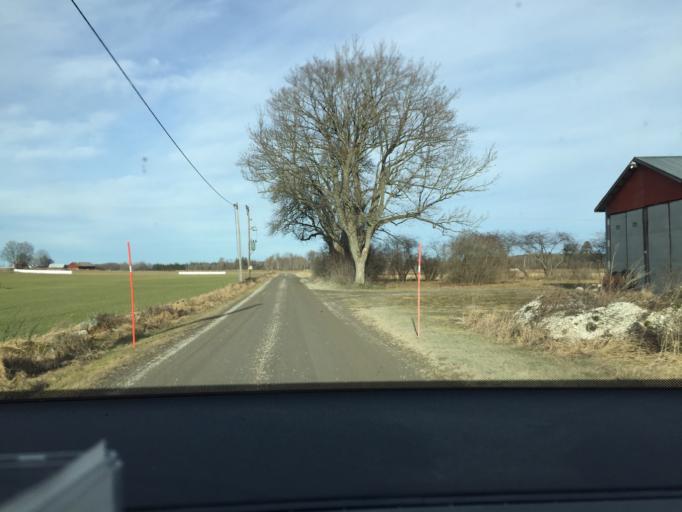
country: SE
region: OErebro
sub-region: Hallsbergs Kommun
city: Skollersta
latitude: 59.1332
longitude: 15.4288
